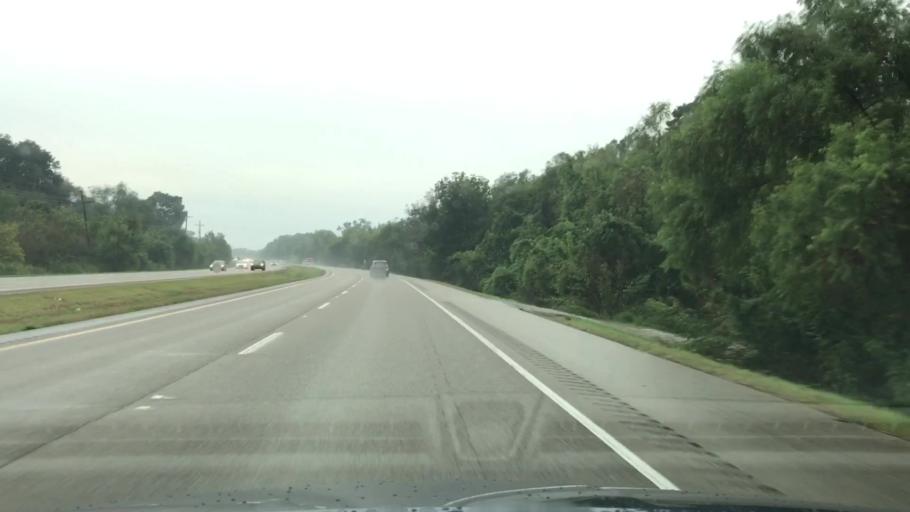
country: US
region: Louisiana
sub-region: Saint Charles Parish
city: Paradis
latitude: 29.8557
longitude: -90.4478
